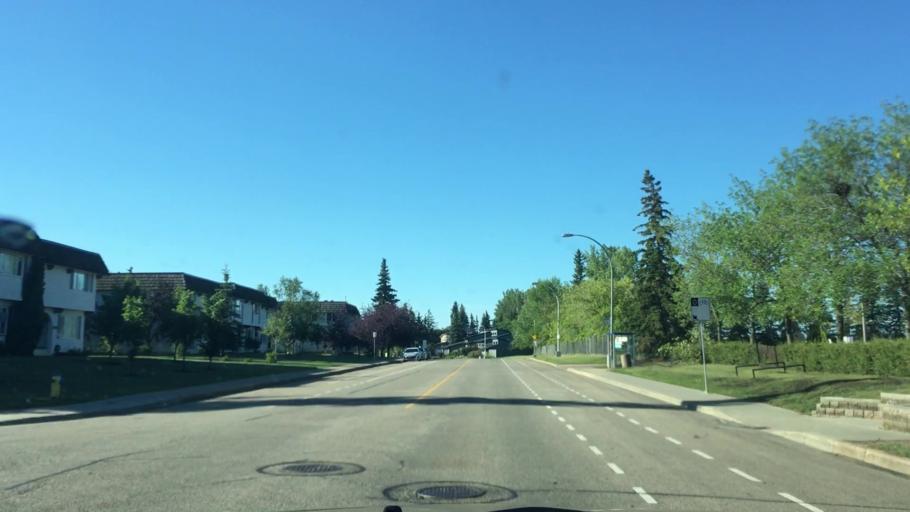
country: CA
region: Alberta
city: Edmonton
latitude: 53.4527
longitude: -113.5256
